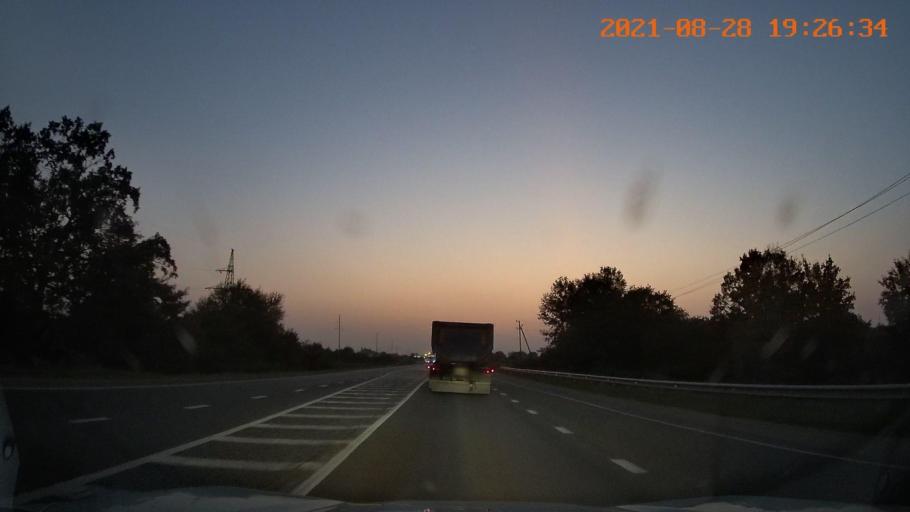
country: RU
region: Adygeya
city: Ponezhukay
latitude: 44.8785
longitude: 39.3931
